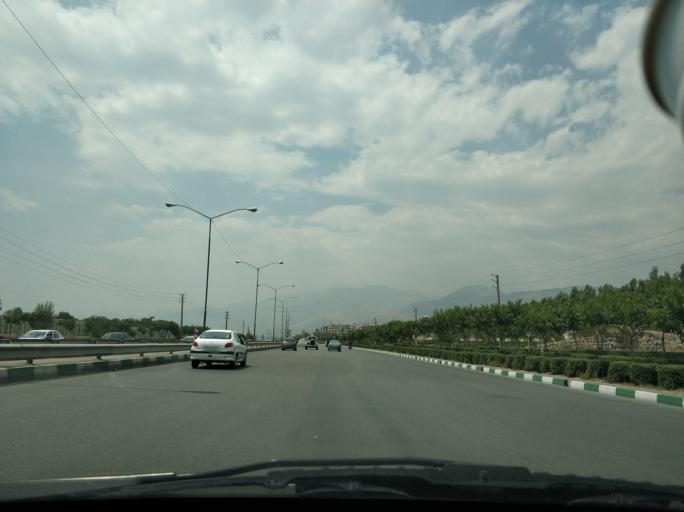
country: IR
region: Tehran
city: Tajrish
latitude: 35.7628
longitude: 51.5688
